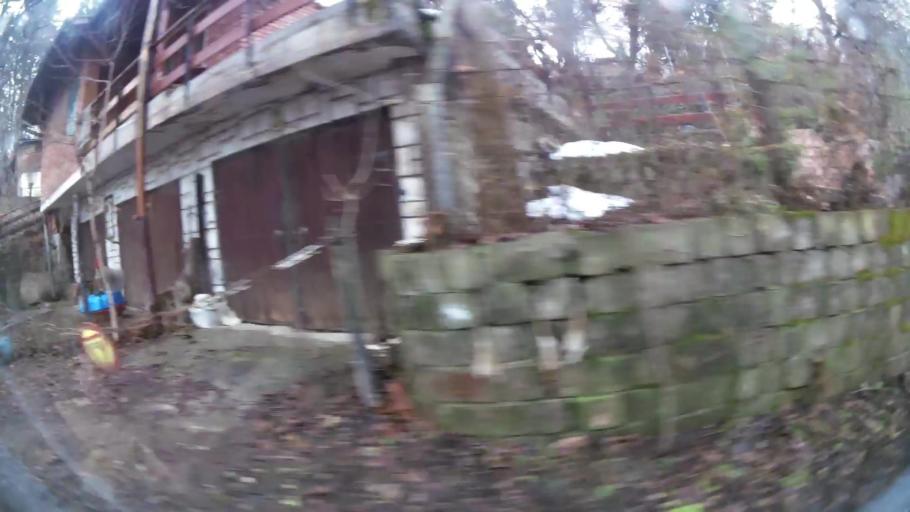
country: BG
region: Sofia-Capital
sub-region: Stolichna Obshtina
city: Sofia
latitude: 42.6010
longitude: 23.3876
